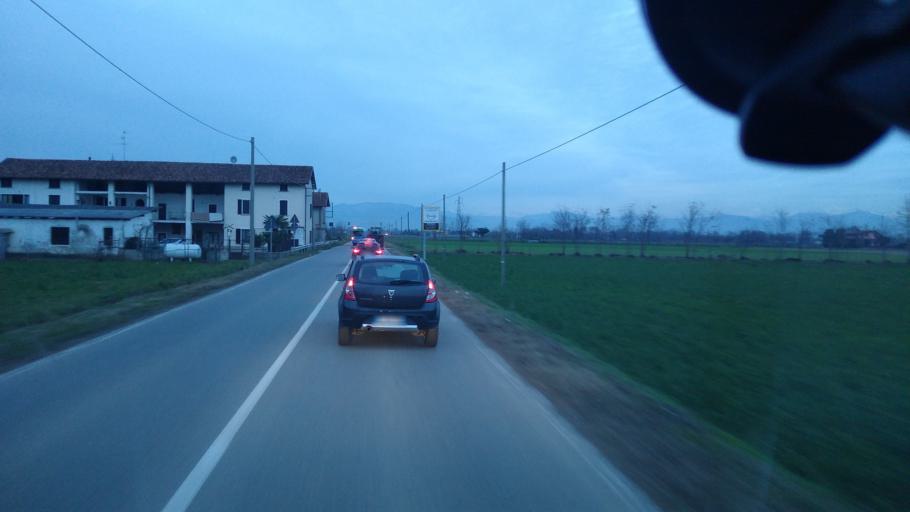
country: IT
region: Lombardy
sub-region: Provincia di Bergamo
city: Pontirolo Nuovo
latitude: 45.5623
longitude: 9.5841
